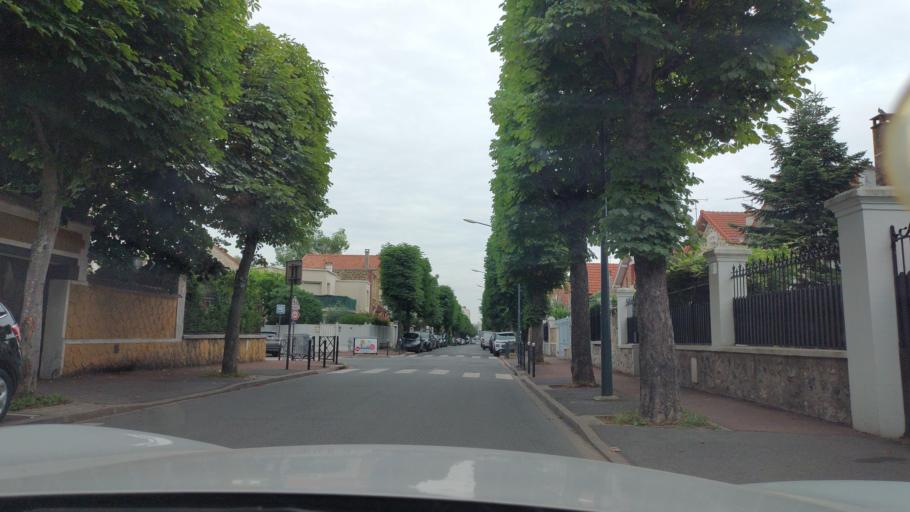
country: FR
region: Ile-de-France
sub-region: Departement du Val-de-Marne
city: Saint-Maur-des-Fosses
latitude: 48.8001
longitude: 2.5123
